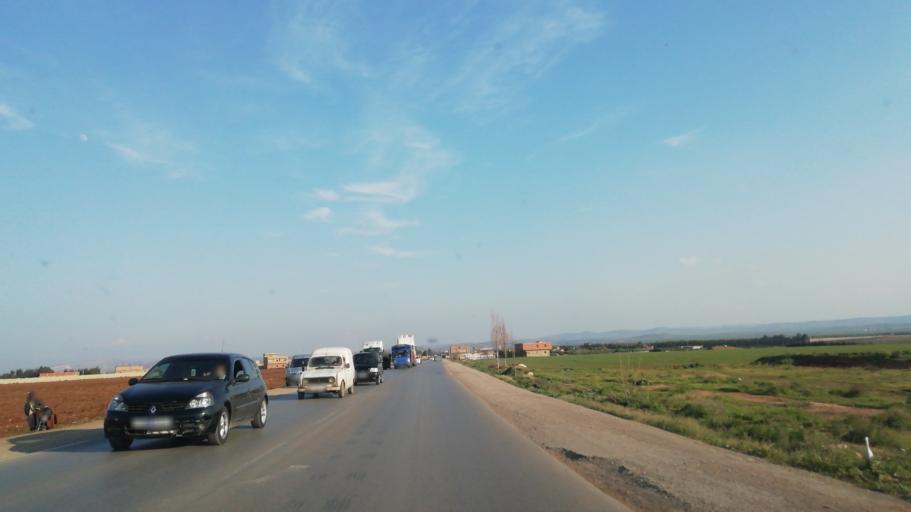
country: DZ
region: Relizane
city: Djidiouia
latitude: 35.8982
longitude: 0.6857
